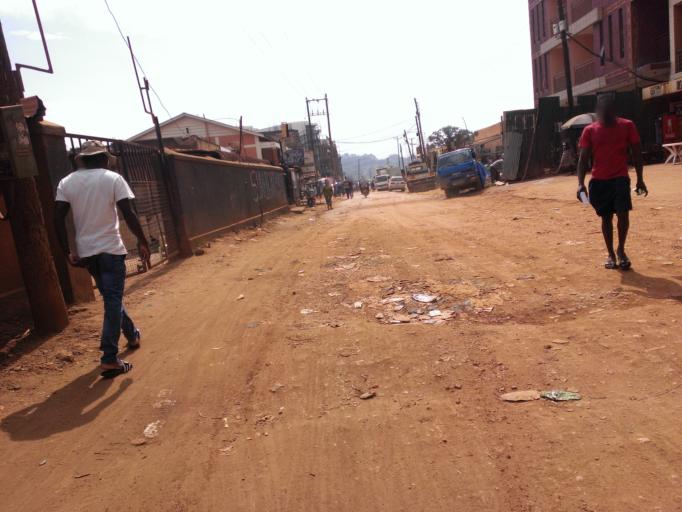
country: UG
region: Central Region
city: Kampala Central Division
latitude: 0.3237
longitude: 32.5591
